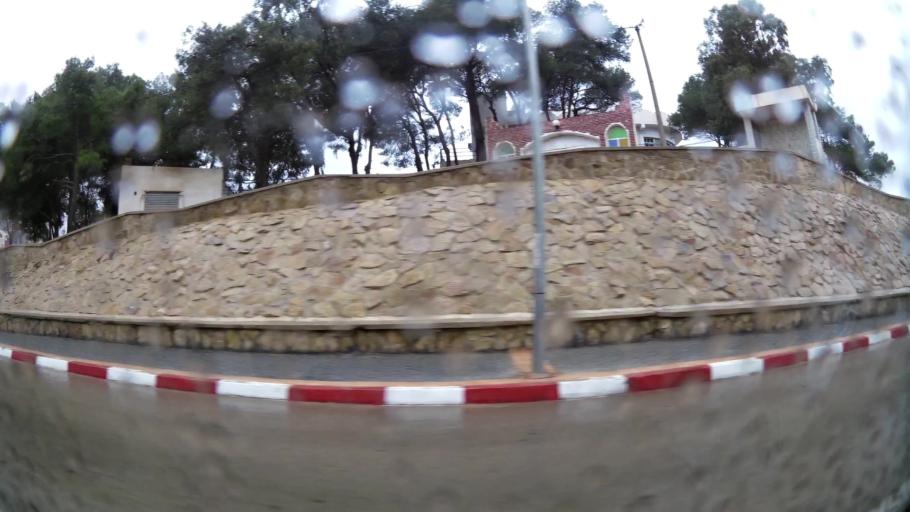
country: MA
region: Taza-Al Hoceima-Taounate
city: Al Hoceima
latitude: 35.2497
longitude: -3.9439
